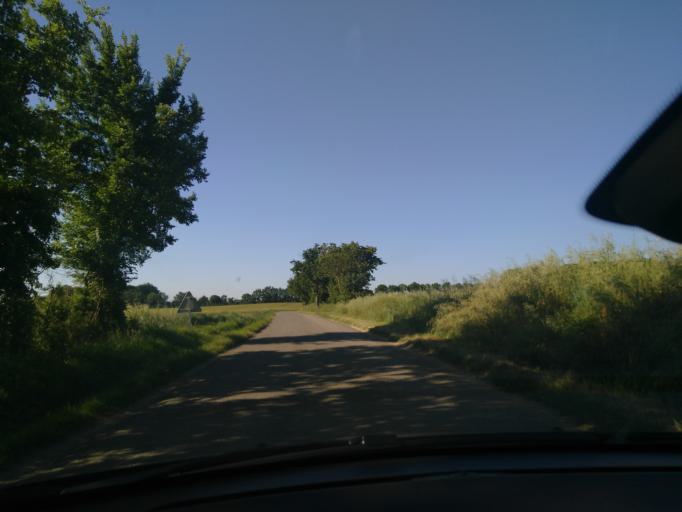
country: FR
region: Midi-Pyrenees
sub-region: Departement du Tarn-et-Garonne
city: Beaumont-de-Lomagne
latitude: 43.7644
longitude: 0.9221
